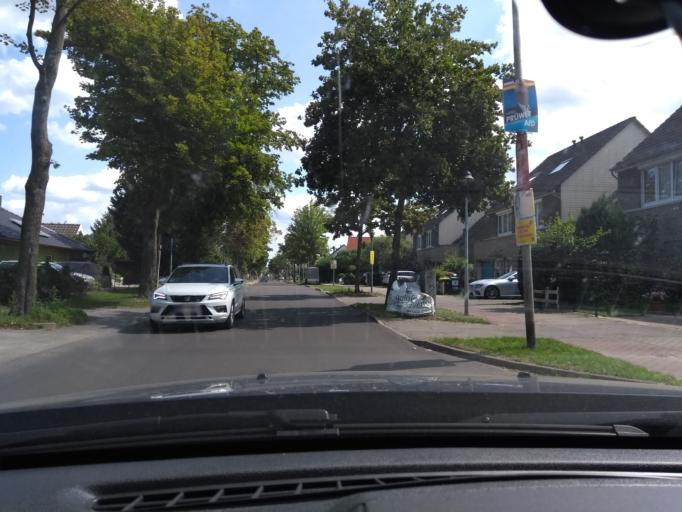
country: DE
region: Brandenburg
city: Dallgow-Doeberitz
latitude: 52.5631
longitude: 13.0623
